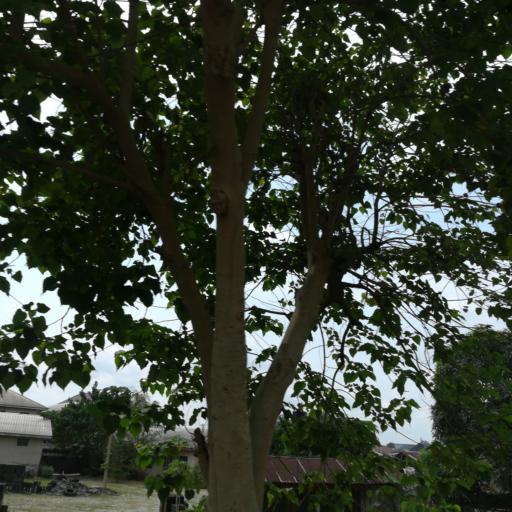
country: NG
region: Rivers
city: Port Harcourt
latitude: 4.8746
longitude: 7.0132
